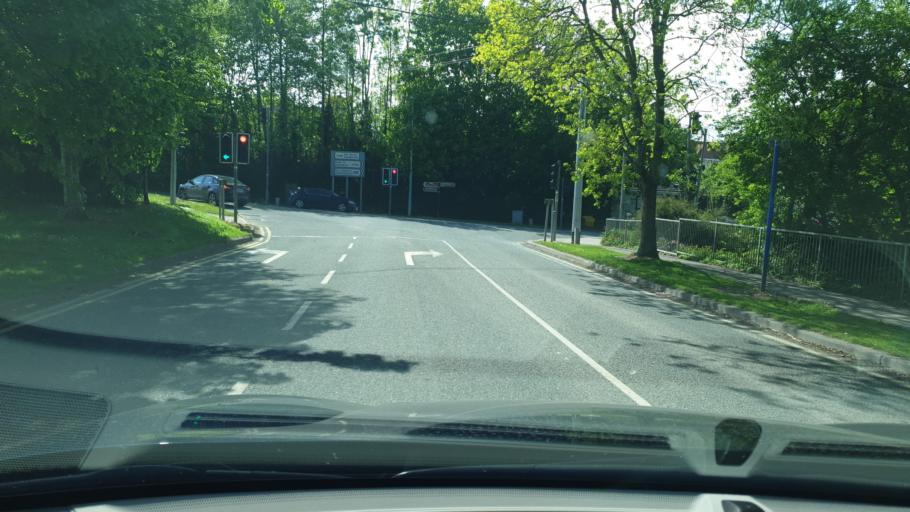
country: IE
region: Leinster
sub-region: An Mhi
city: Ratoath
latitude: 53.5044
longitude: -6.4659
